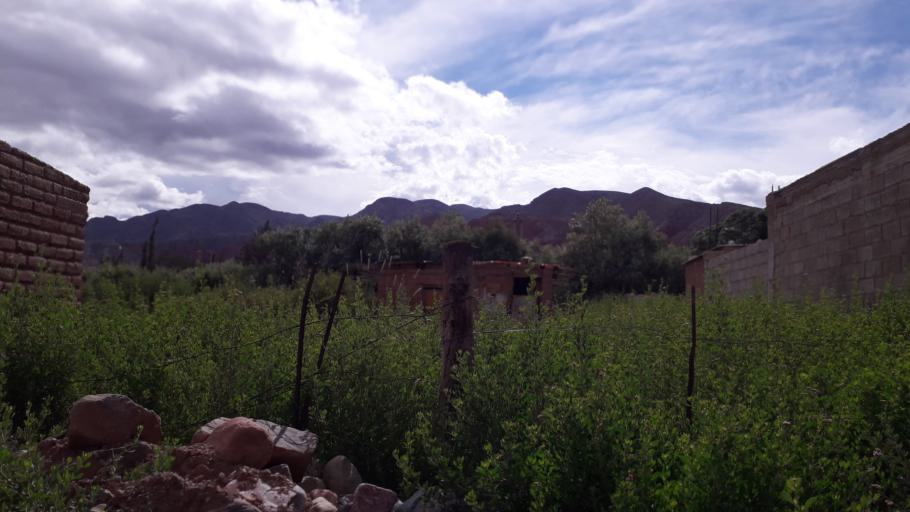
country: AR
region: Jujuy
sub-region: Departamento de Humahuaca
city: Humahuaca
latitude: -23.3047
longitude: -65.3539
